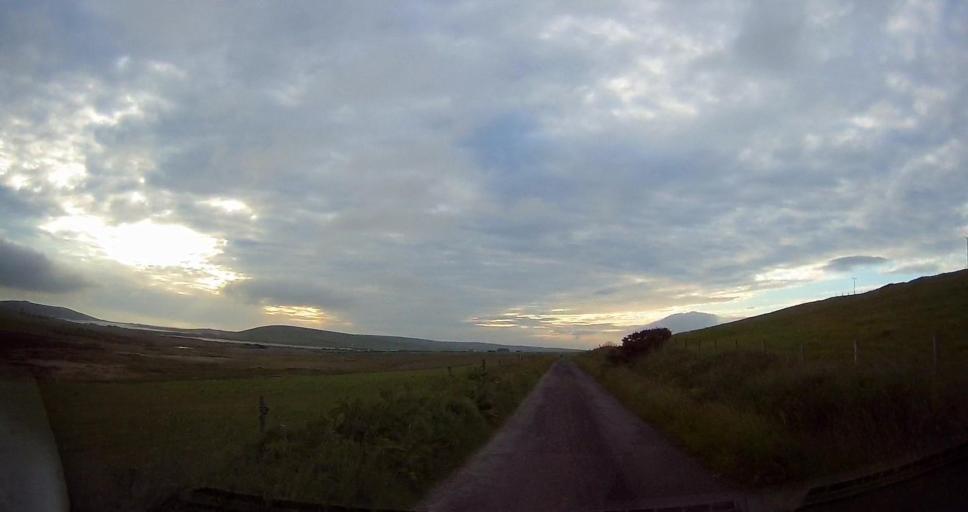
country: GB
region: Scotland
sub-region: Orkney Islands
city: Stromness
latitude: 59.1028
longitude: -3.2112
